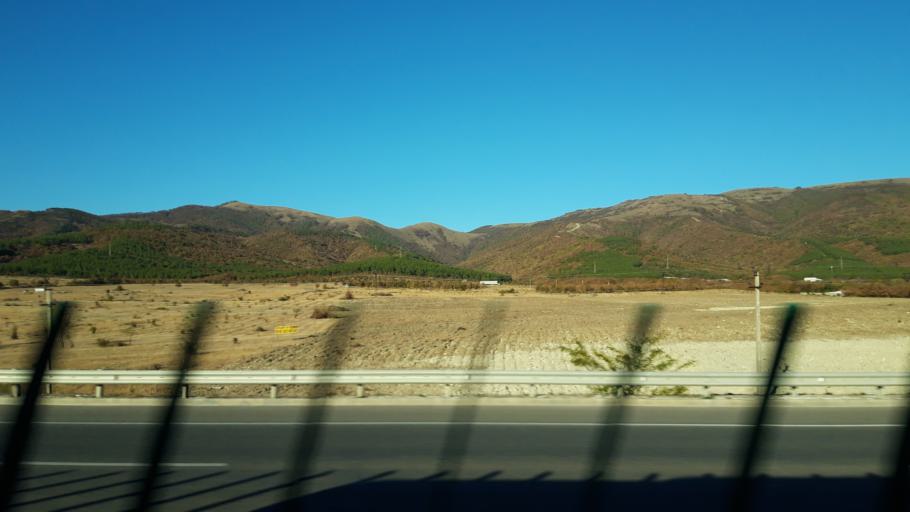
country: RU
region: Krasnodarskiy
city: Kabardinka
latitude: 44.6359
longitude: 37.9929
